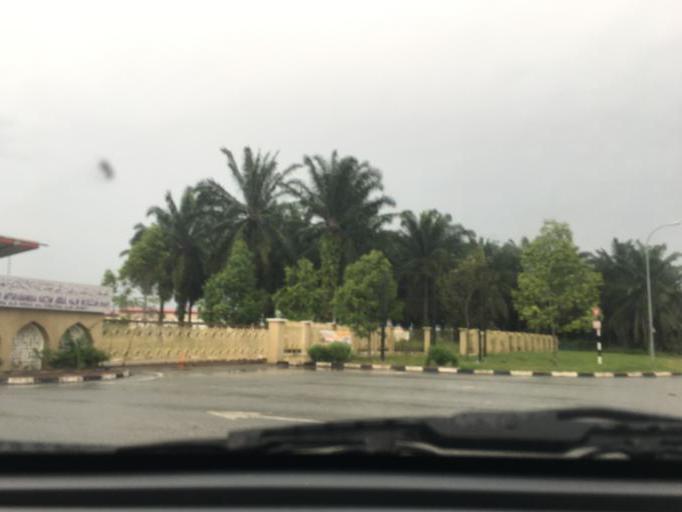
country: MY
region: Kedah
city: Sungai Petani
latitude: 5.5900
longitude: 100.6393
